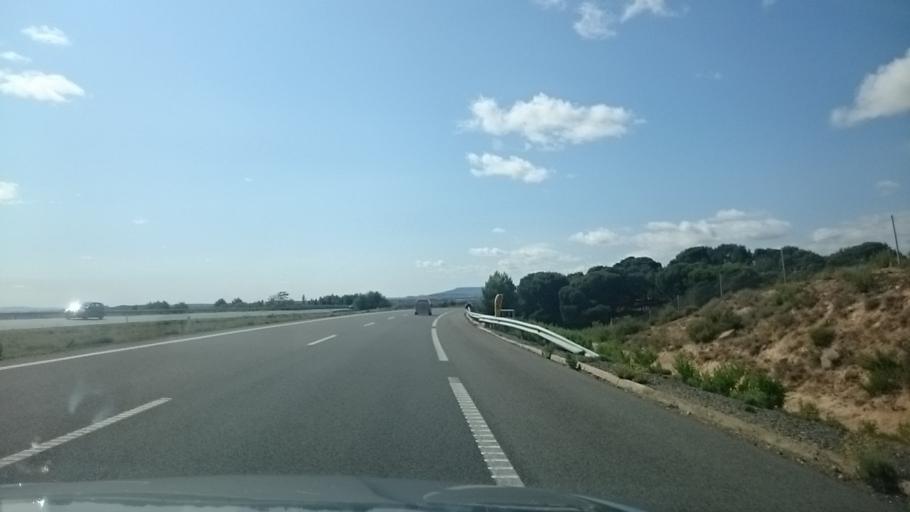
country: ES
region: Navarre
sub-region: Provincia de Navarra
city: Murchante
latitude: 42.0723
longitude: -1.6933
